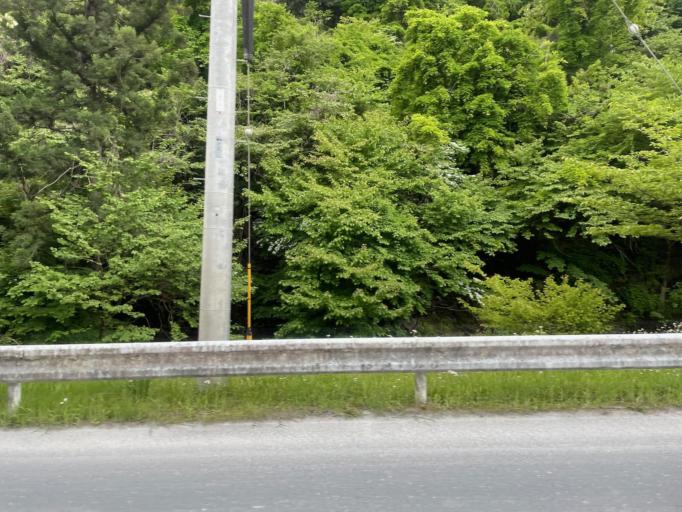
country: JP
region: Tochigi
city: Tanuma
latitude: 36.4568
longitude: 139.6069
